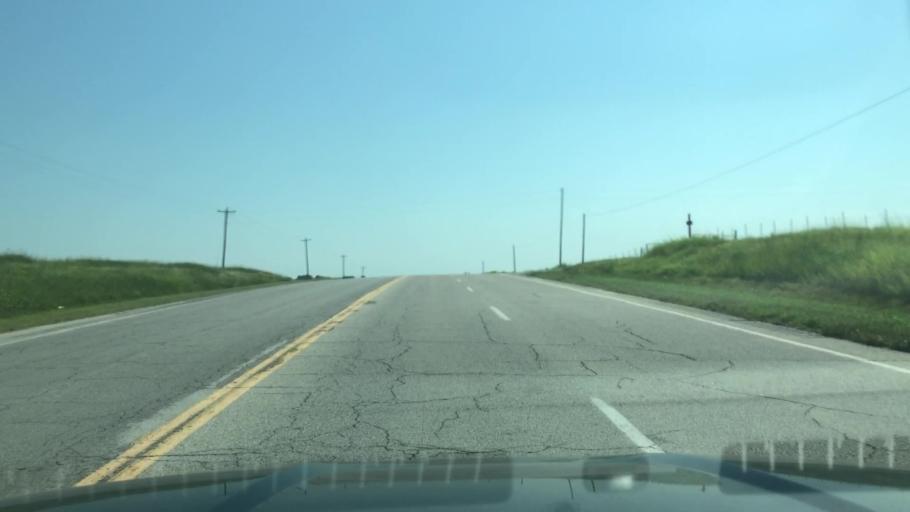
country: US
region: Oklahoma
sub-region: Creek County
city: Drumright
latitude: 35.9930
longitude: -96.5350
